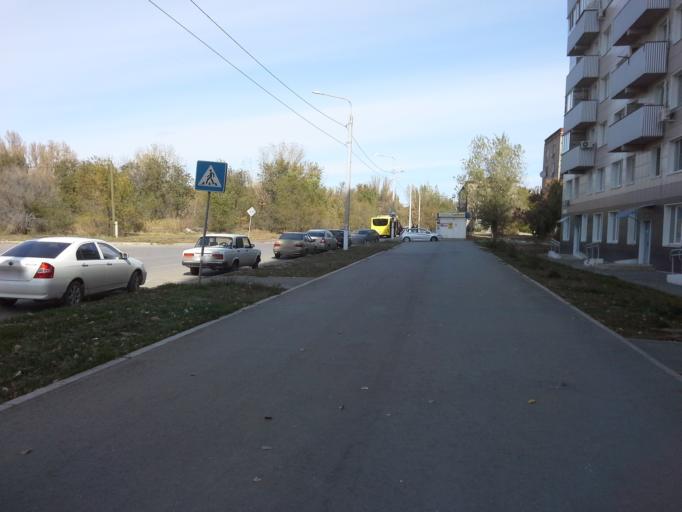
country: RU
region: Volgograd
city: Vodstroy
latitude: 48.8384
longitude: 44.6374
